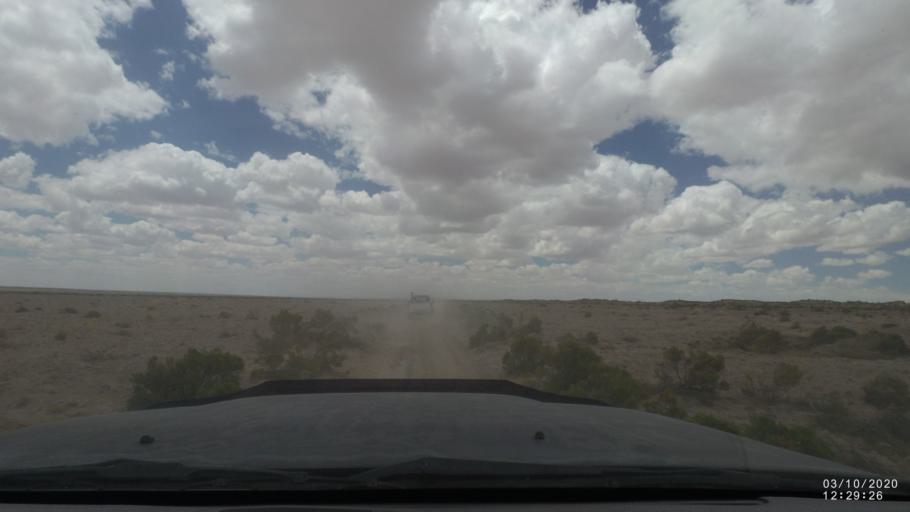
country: BO
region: Oruro
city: Poopo
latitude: -18.6891
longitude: -67.5479
